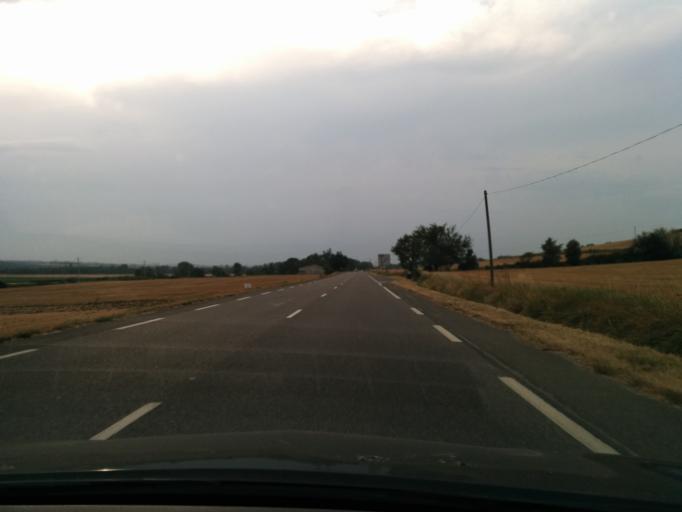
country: FR
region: Midi-Pyrenees
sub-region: Departement de la Haute-Garonne
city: Villenouvelle
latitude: 43.4438
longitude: 1.6425
